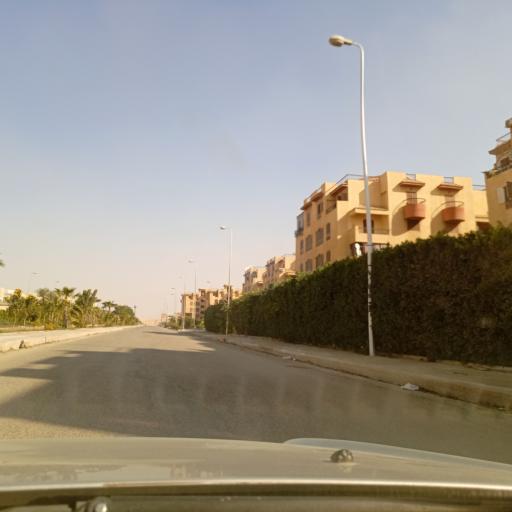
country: EG
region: Muhafazat al Qalyubiyah
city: Al Khankah
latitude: 30.0457
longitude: 31.4866
